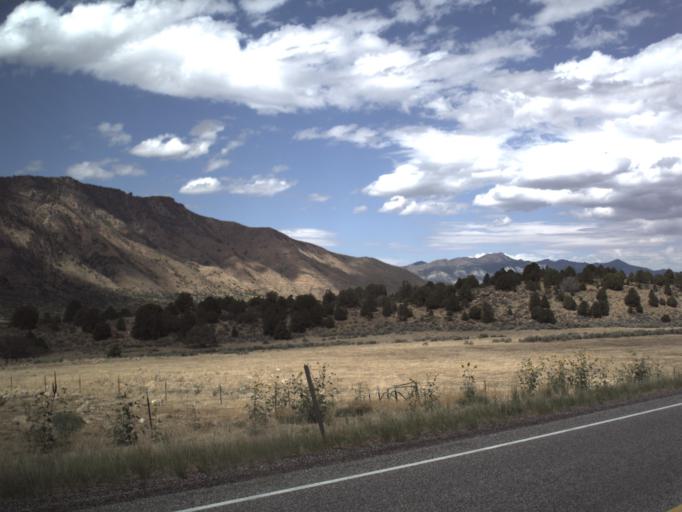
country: US
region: Utah
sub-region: Sanpete County
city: Gunnison
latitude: 39.1671
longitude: -112.0742
